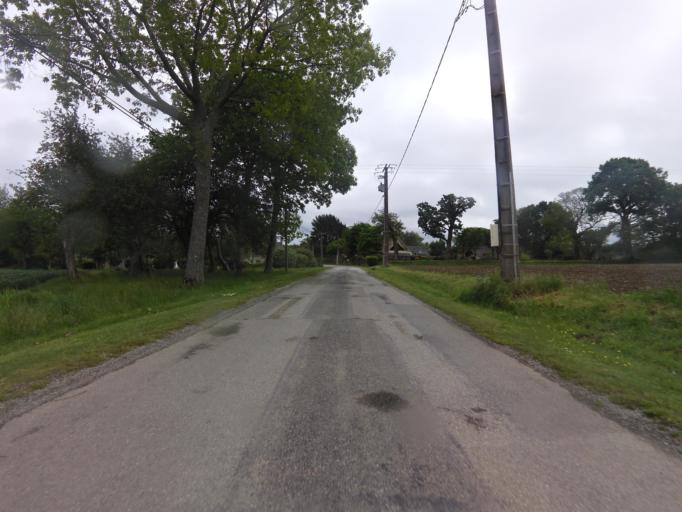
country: FR
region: Brittany
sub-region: Departement du Morbihan
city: Plougoumelen
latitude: 47.6360
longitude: -2.9116
